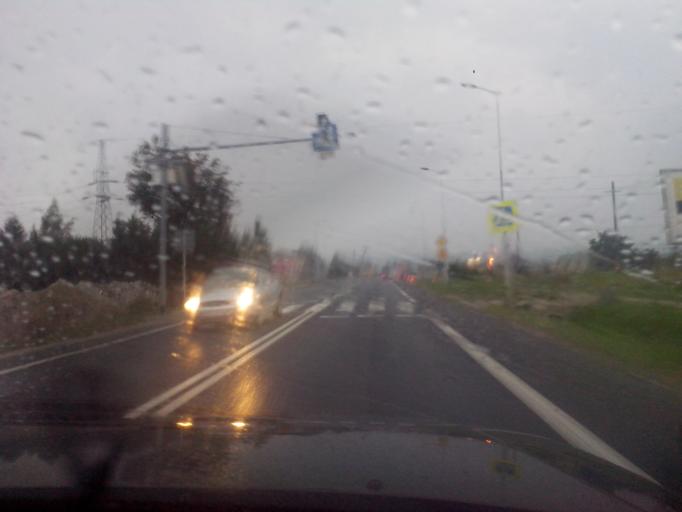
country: PL
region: Subcarpathian Voivodeship
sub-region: Powiat rzeszowski
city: Boguchwala
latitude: 49.9970
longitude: 21.9574
